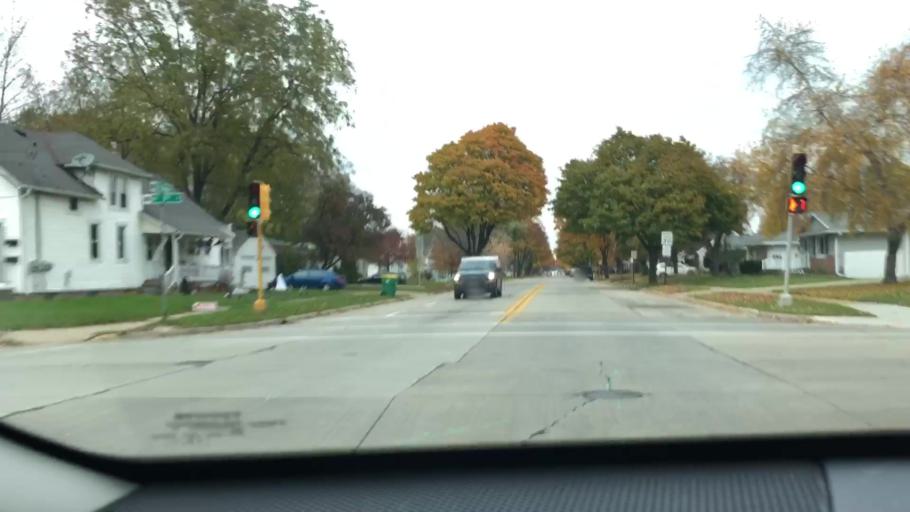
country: US
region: Wisconsin
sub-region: Brown County
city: Green Bay
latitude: 44.5098
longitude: -88.0514
